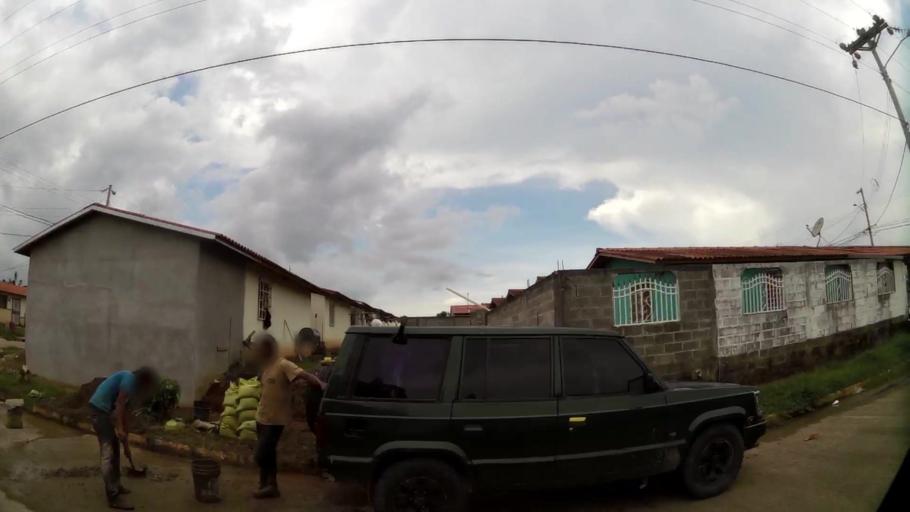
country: PA
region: Panama
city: Cabra Numero Uno
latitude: 9.1172
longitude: -79.3209
